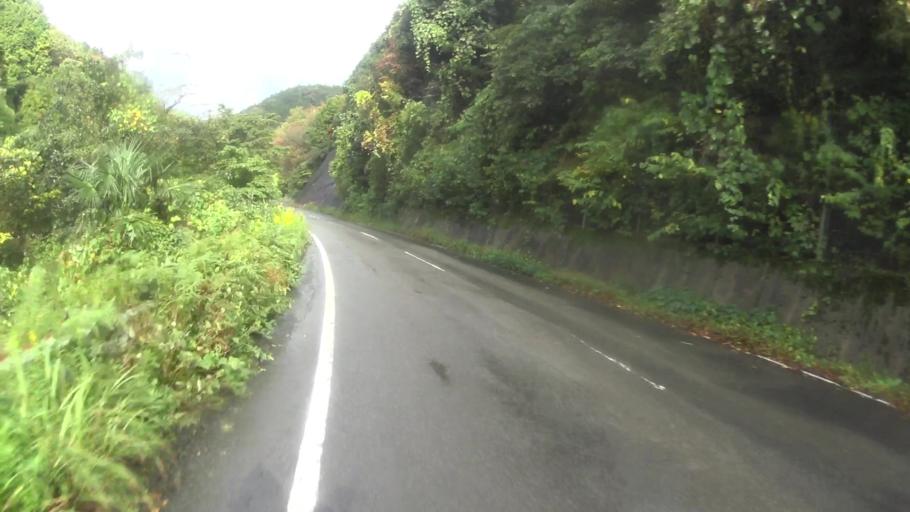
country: JP
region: Kyoto
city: Ayabe
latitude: 35.3746
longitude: 135.1874
